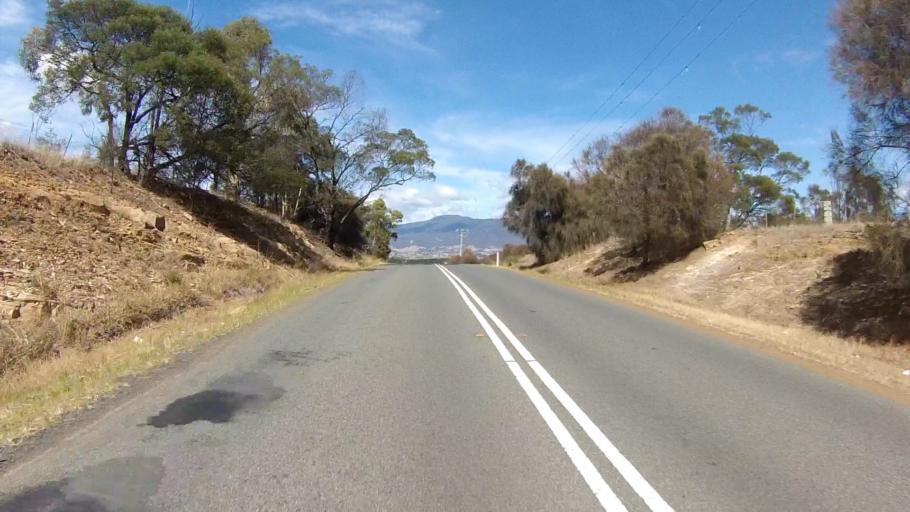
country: AU
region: Tasmania
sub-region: Brighton
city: Bridgewater
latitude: -42.7070
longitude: 147.2701
